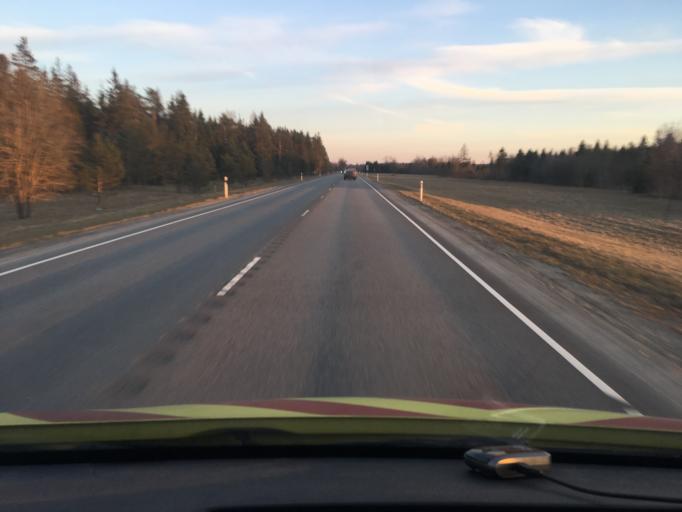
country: EE
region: Raplamaa
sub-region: Kohila vald
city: Kohila
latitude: 59.2082
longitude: 24.7797
